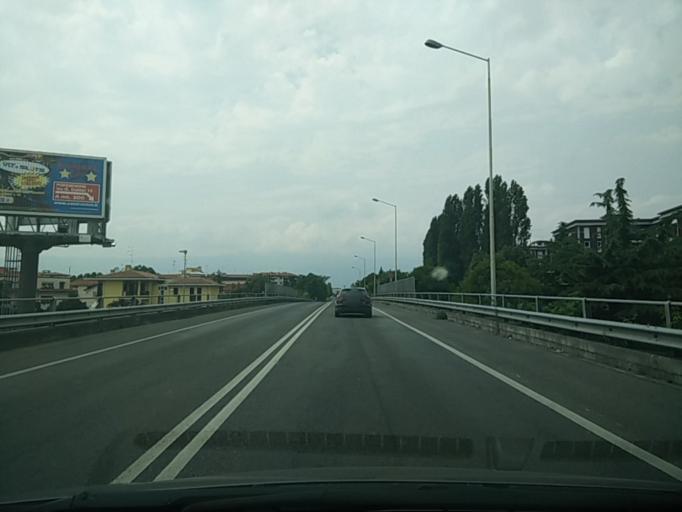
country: IT
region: Friuli Venezia Giulia
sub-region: Provincia di Pordenone
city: Pordenone
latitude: 45.9677
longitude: 12.6692
